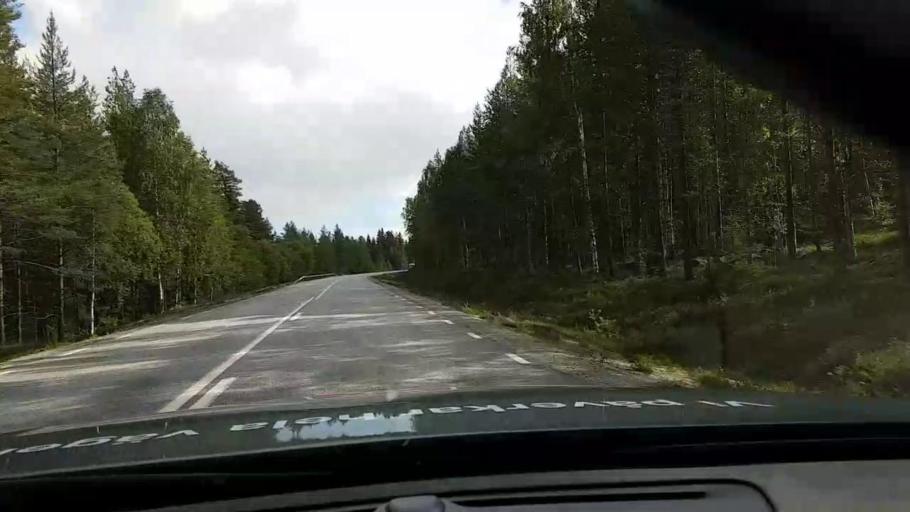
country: SE
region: Vaesternorrland
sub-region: OErnskoeldsviks Kommun
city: Bredbyn
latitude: 63.6349
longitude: 17.9063
